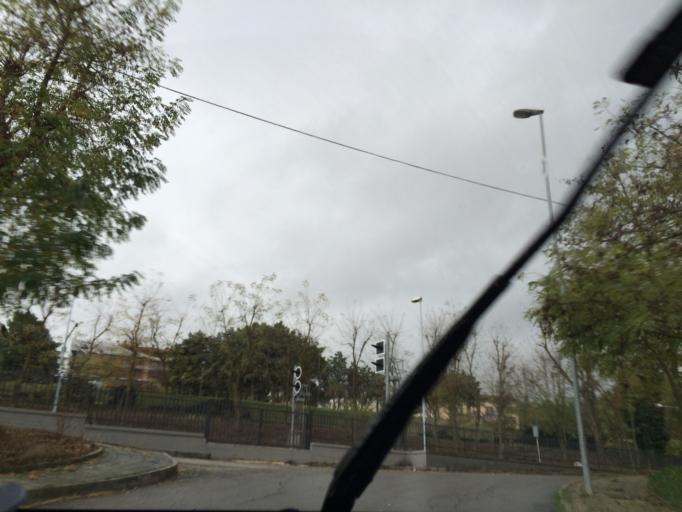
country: IT
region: Basilicate
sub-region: Provincia di Matera
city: Matera
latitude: 40.6608
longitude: 16.6041
